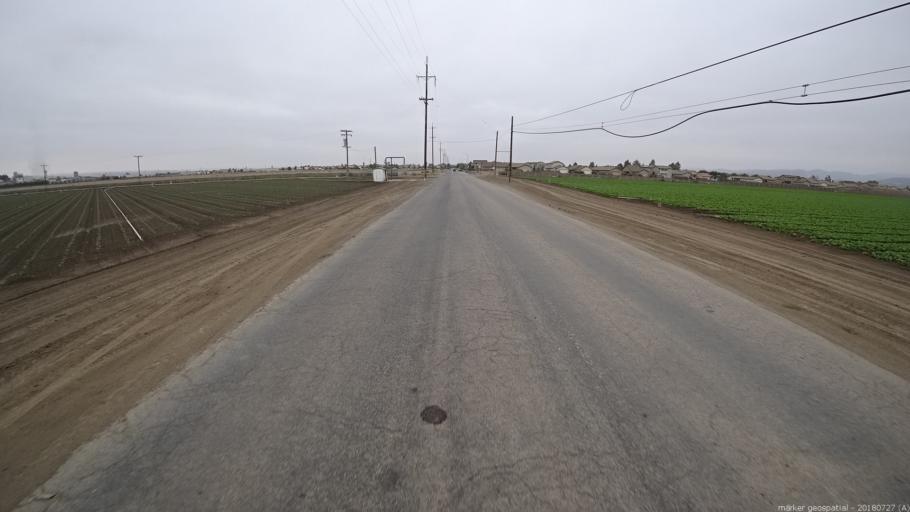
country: US
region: California
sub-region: Monterey County
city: King City
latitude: 36.2252
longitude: -121.1368
